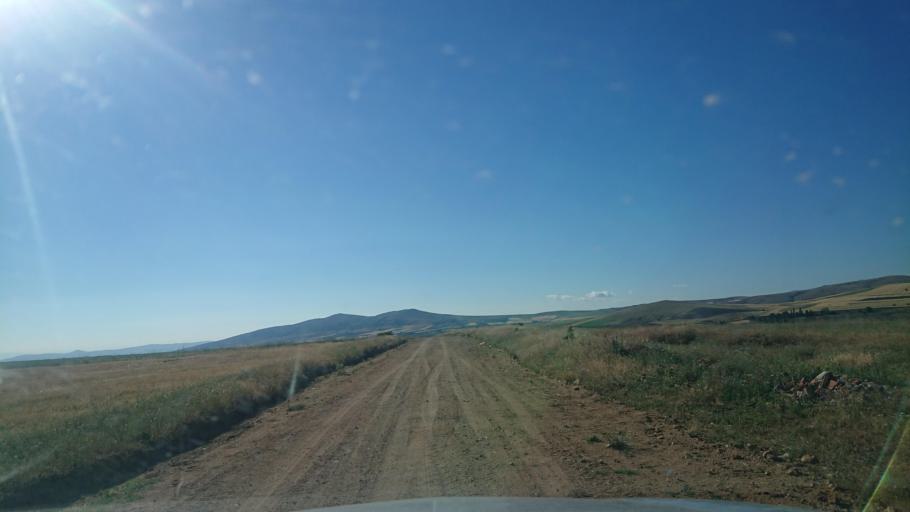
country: TR
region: Aksaray
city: Agacoren
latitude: 38.8283
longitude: 33.9530
